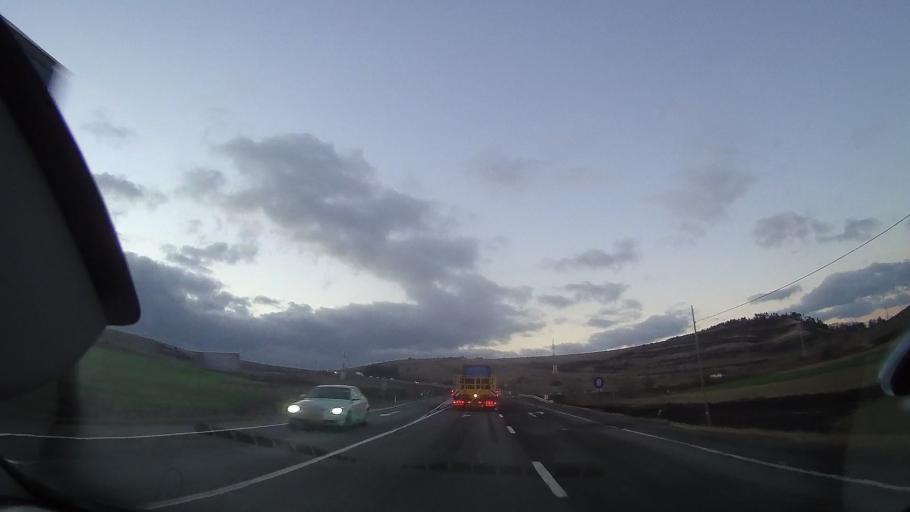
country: RO
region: Cluj
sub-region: Comuna Izvoru Crisului
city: Izvoru Crisului
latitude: 46.8213
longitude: 23.1681
